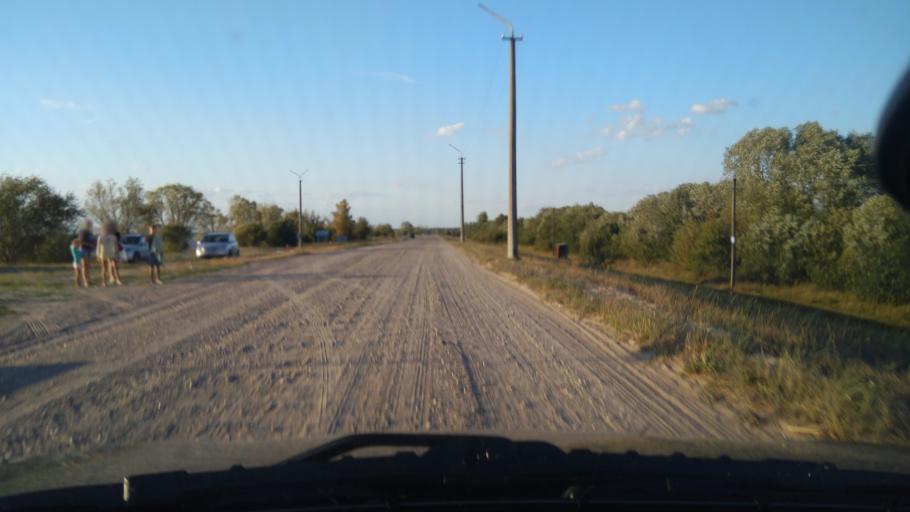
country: BY
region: Brest
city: Byaroza
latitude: 52.6077
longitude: 24.8801
